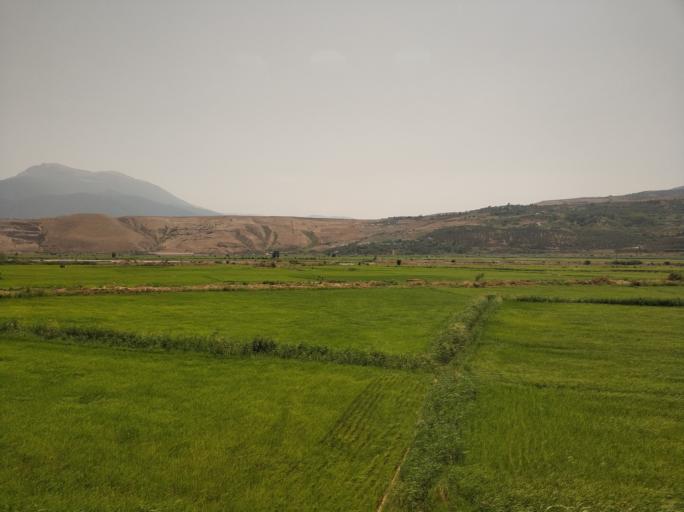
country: IR
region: Gilan
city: Pa'in-e Bazar-e Rudbar
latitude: 36.8805
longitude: 49.4973
